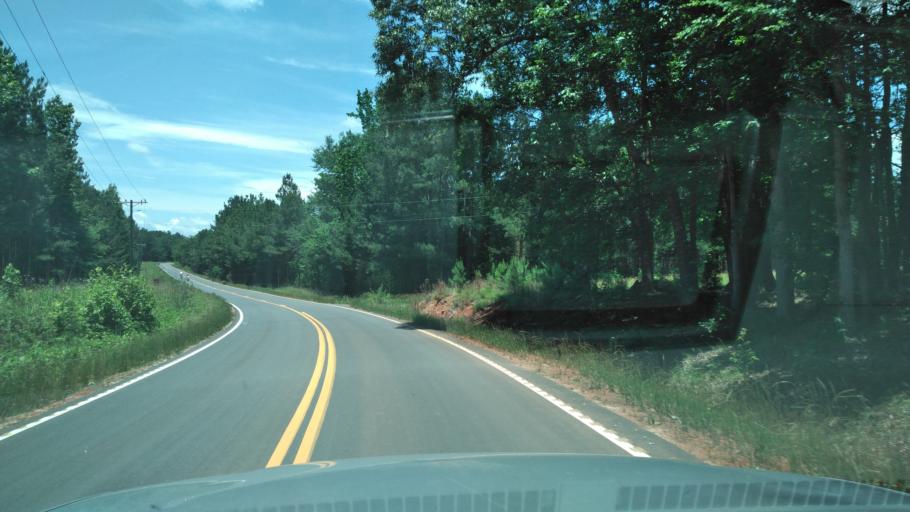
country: US
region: South Carolina
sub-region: Greenwood County
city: Ware Shoals
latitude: 34.3943
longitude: -82.1174
